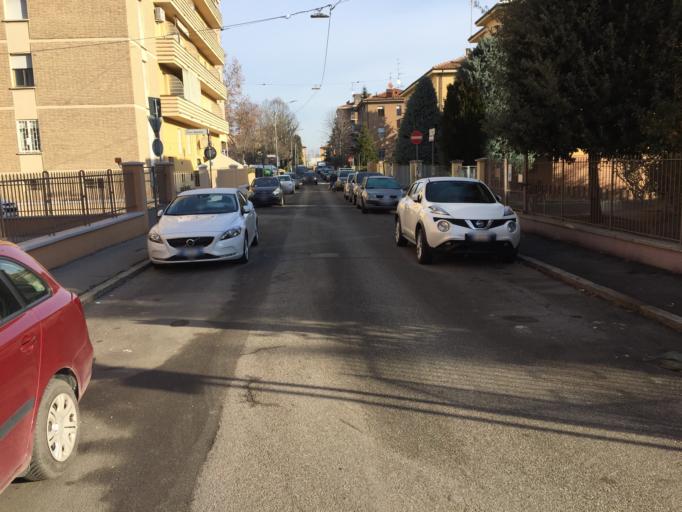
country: IT
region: Emilia-Romagna
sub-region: Provincia di Bologna
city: Casalecchio di Reno
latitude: 44.5192
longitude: 11.2741
